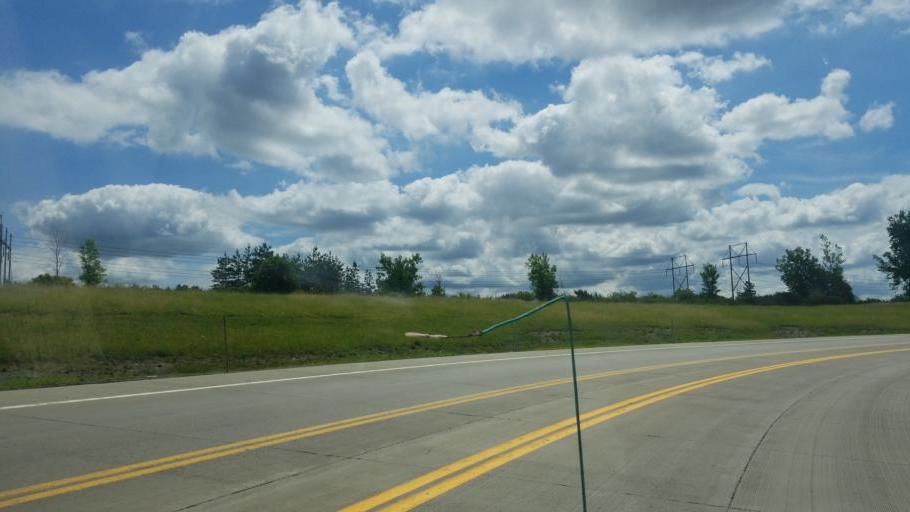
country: US
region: New York
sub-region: Erie County
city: Blasdell
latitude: 42.7953
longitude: -78.8142
